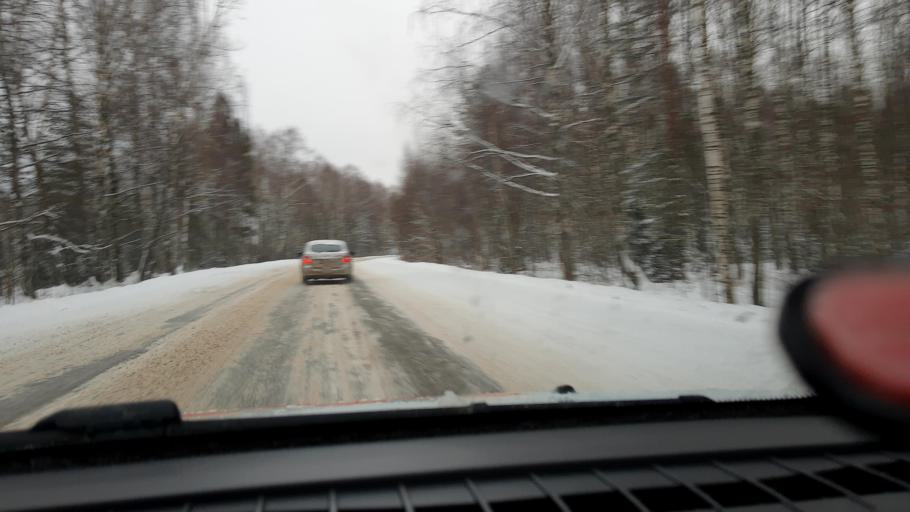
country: RU
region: Nizjnij Novgorod
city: Pamyat' Parizhskoy Kommuny
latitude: 56.2560
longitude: 44.4655
